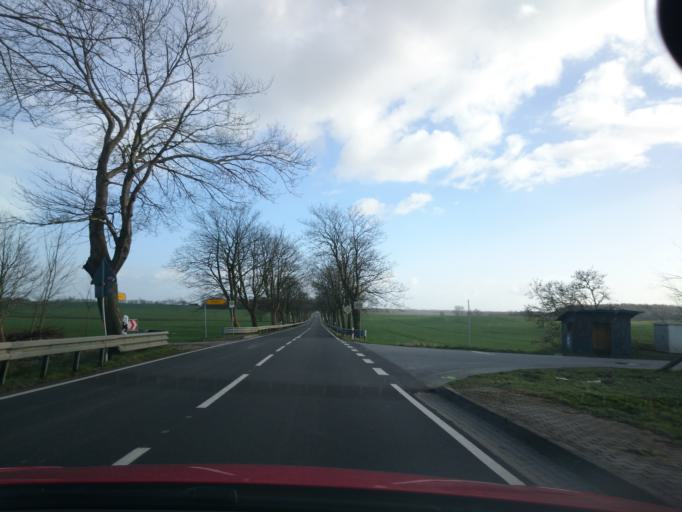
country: DE
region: Mecklenburg-Vorpommern
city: Barth
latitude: 54.3126
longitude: 12.7172
